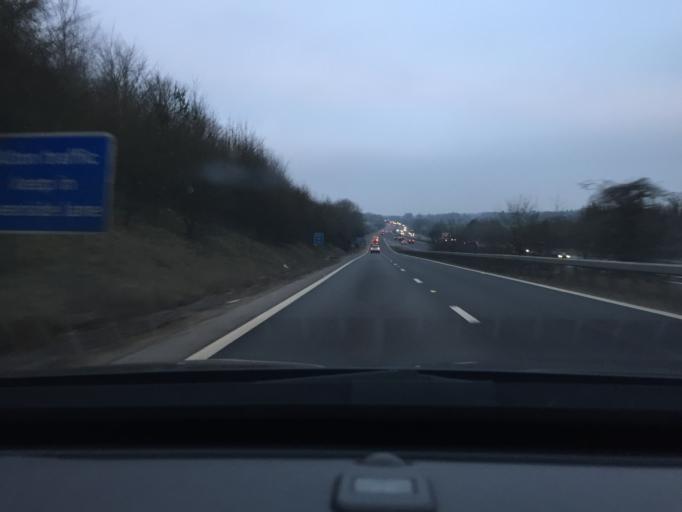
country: GB
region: England
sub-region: Hampshire
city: Fareham
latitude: 50.8606
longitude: -1.1611
